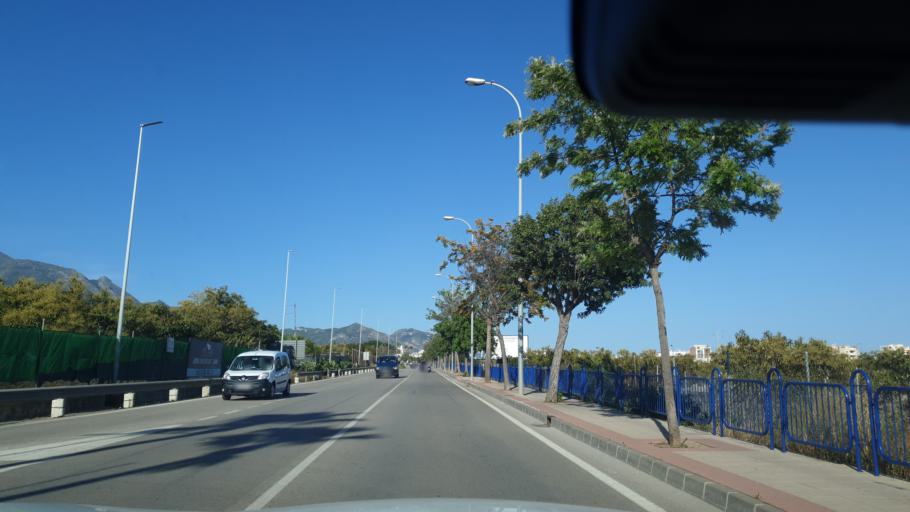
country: ES
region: Andalusia
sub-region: Provincia de Malaga
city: Nerja
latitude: 36.7468
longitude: -3.8906
